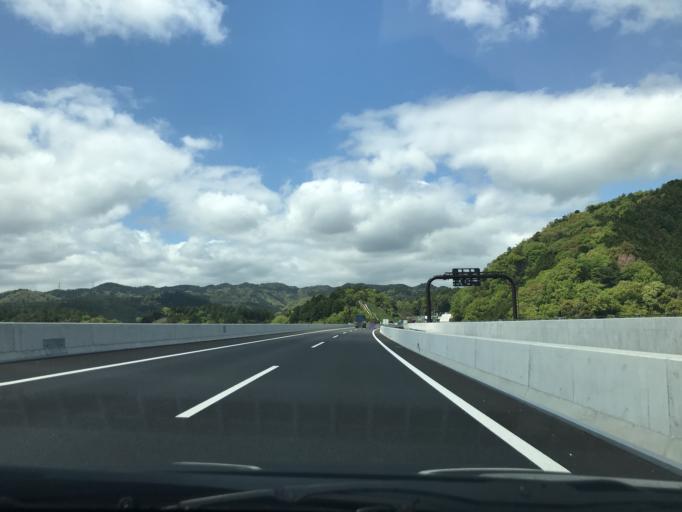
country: JP
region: Osaka
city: Takatsuki
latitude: 34.8891
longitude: 135.6121
